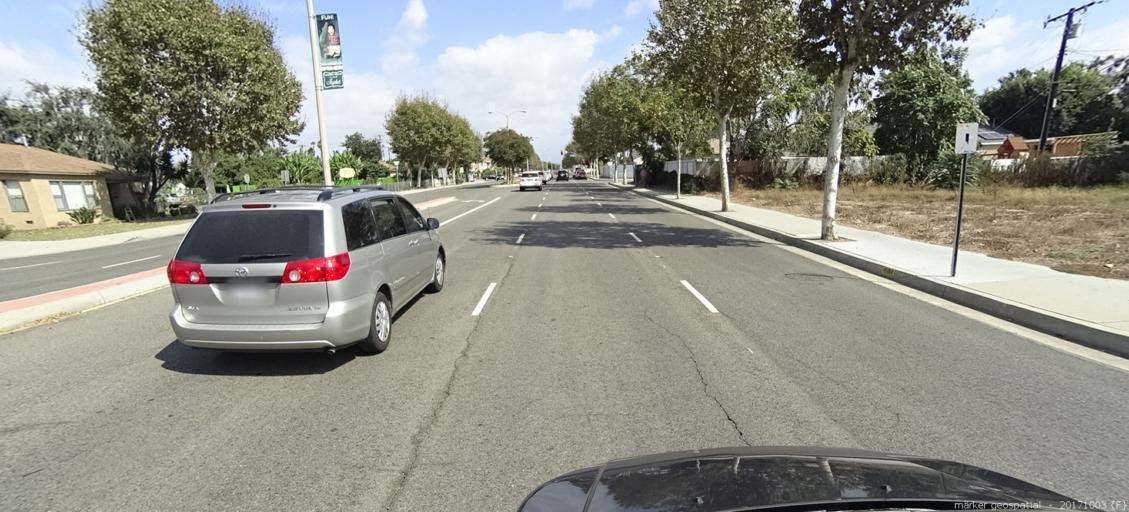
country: US
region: California
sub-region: Orange County
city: Garden Grove
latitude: 33.7742
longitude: -117.9339
